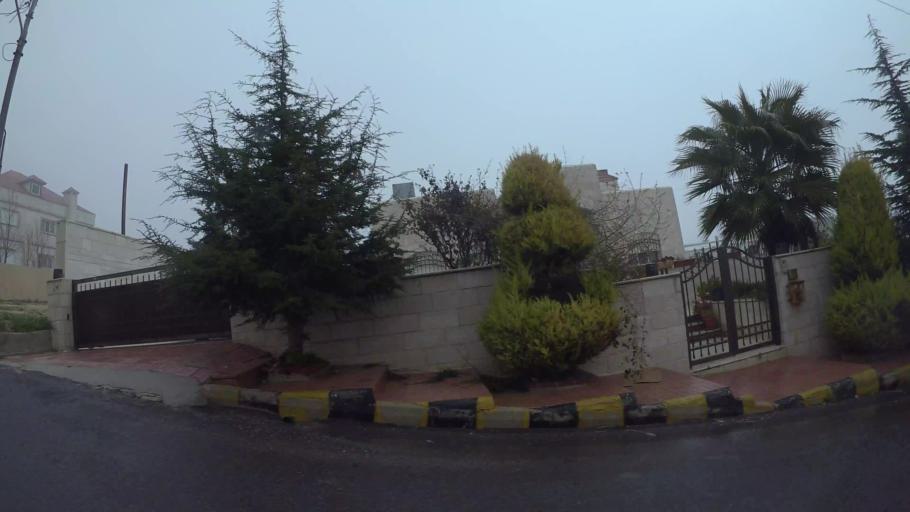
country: JO
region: Amman
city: Al Jubayhah
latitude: 32.0126
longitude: 35.8376
